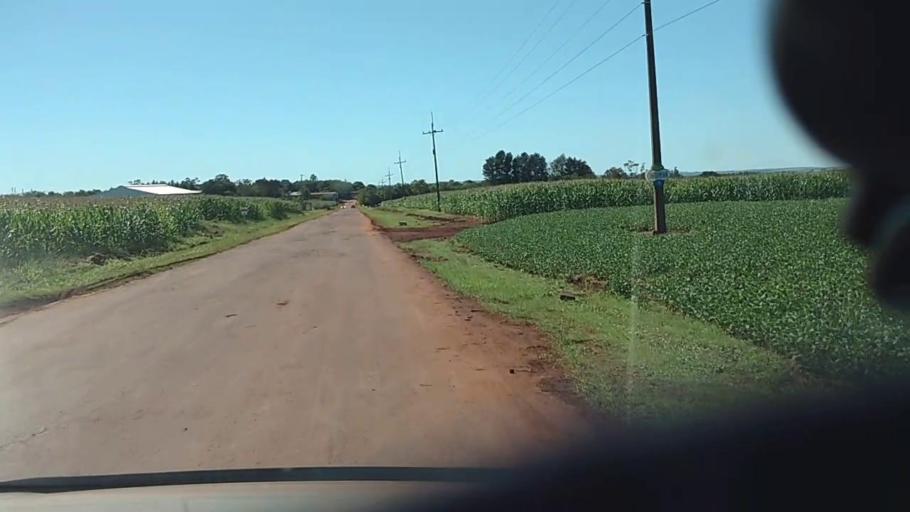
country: PY
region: Alto Parana
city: Naranjal
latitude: -25.9540
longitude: -55.1318
